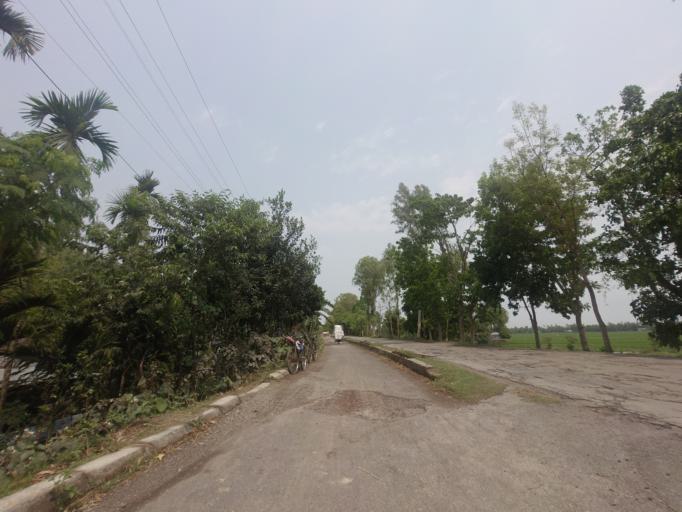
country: BD
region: Rajshahi
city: Sirajganj
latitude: 24.3318
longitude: 89.7003
